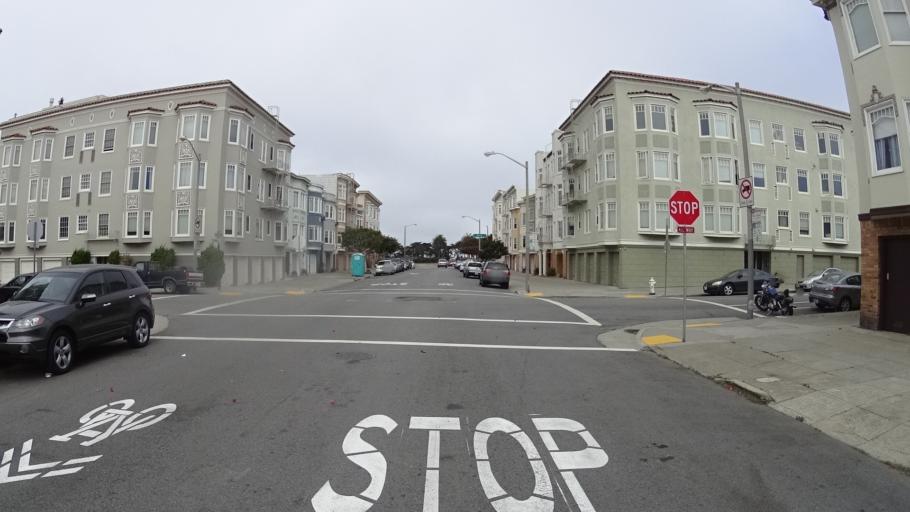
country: US
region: California
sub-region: San Francisco County
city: San Francisco
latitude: 37.8024
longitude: -122.4298
